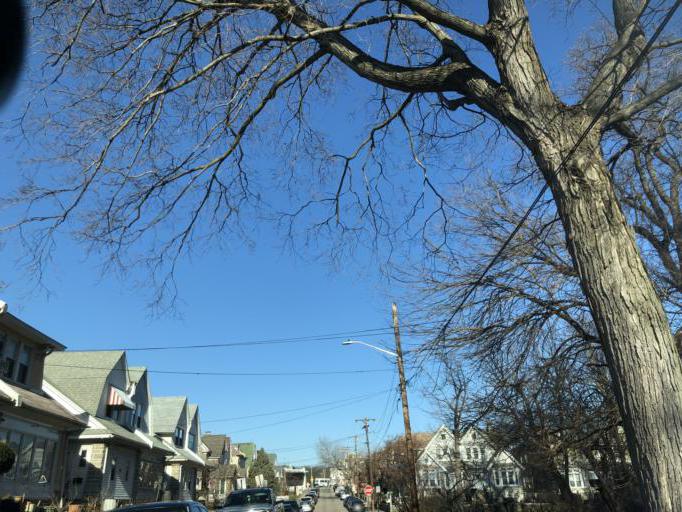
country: US
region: Pennsylvania
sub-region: Delaware County
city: Millbourne
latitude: 39.9607
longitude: -75.2522
